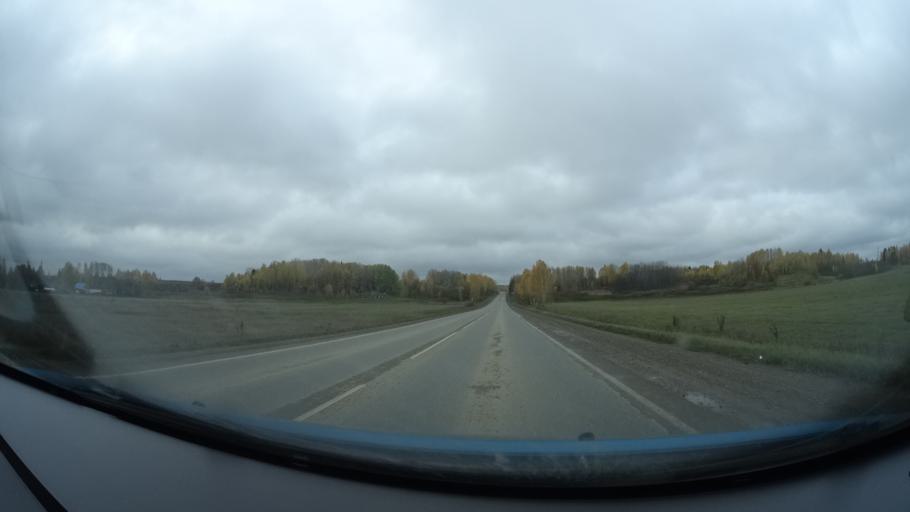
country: RU
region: Perm
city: Osa
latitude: 57.1795
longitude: 55.5531
